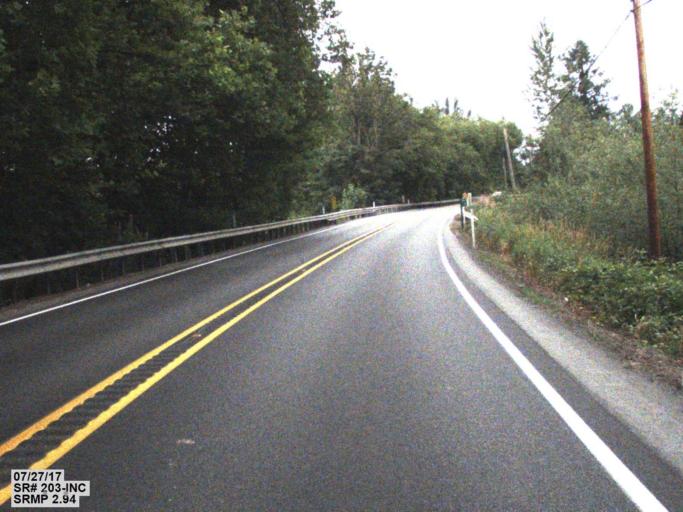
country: US
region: Washington
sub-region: King County
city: Carnation
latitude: 47.6055
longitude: -121.9140
